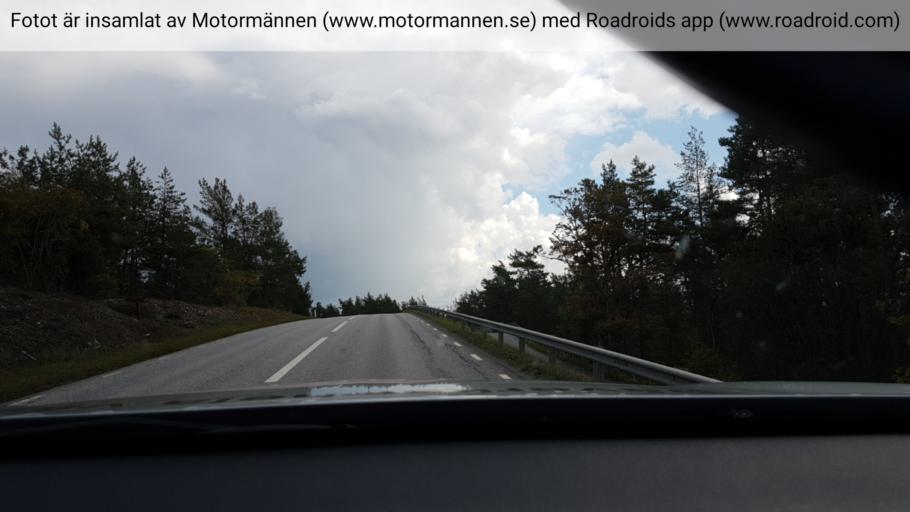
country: SE
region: Stockholm
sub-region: Ekero Kommun
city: Ekeroe
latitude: 59.2787
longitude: 17.7574
